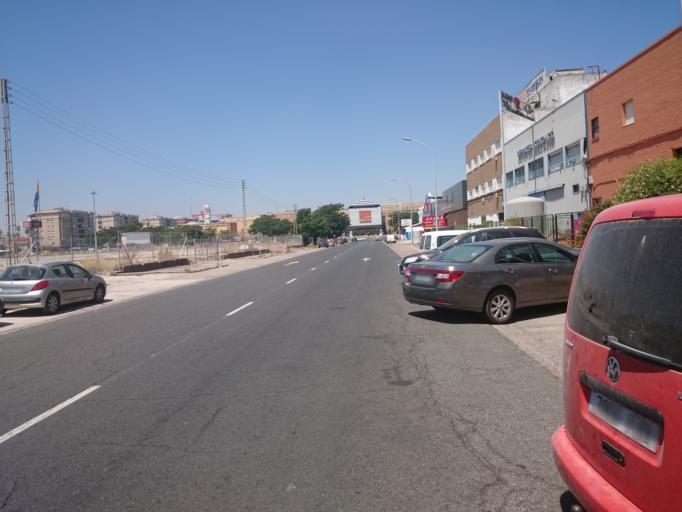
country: ES
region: Andalusia
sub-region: Provincia de Sevilla
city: Sevilla
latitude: 37.3886
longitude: -5.9562
